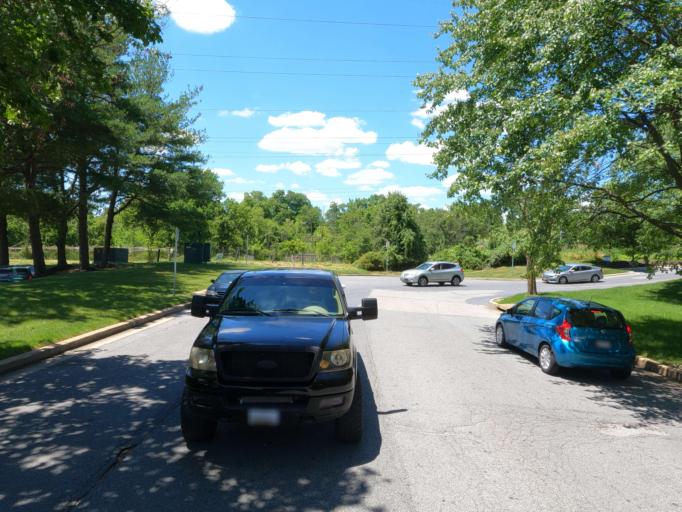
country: US
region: Maryland
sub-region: Howard County
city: Columbia
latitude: 39.1977
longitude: -76.8215
